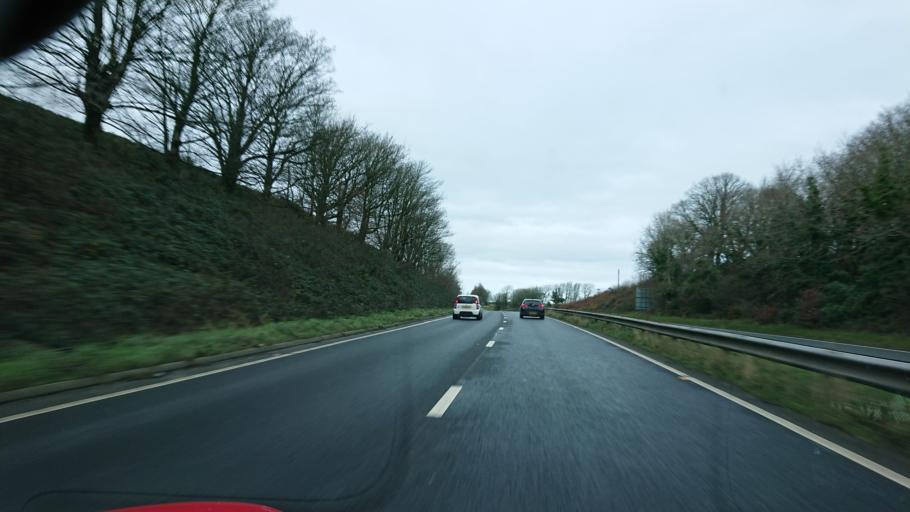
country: GB
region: England
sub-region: Cornwall
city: Liskeard
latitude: 50.4385
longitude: -4.4416
